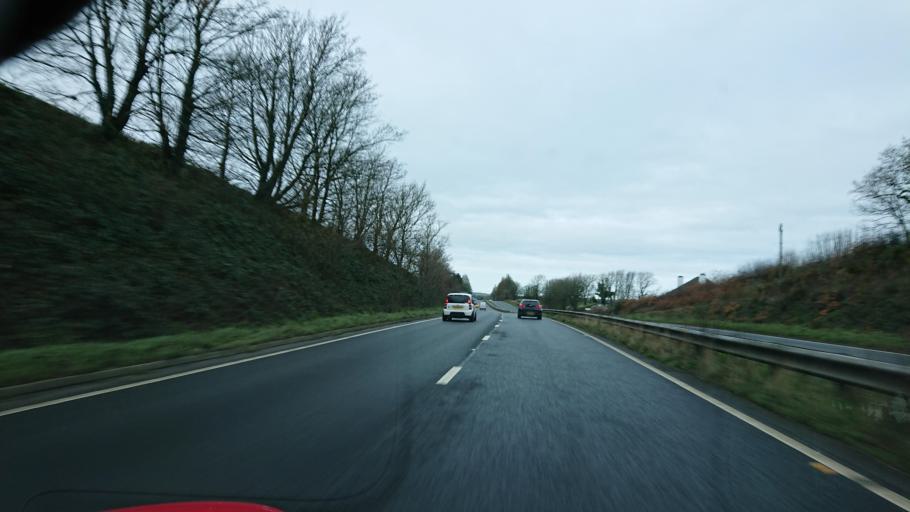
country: GB
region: England
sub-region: Cornwall
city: Liskeard
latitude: 50.4390
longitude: -4.4419
